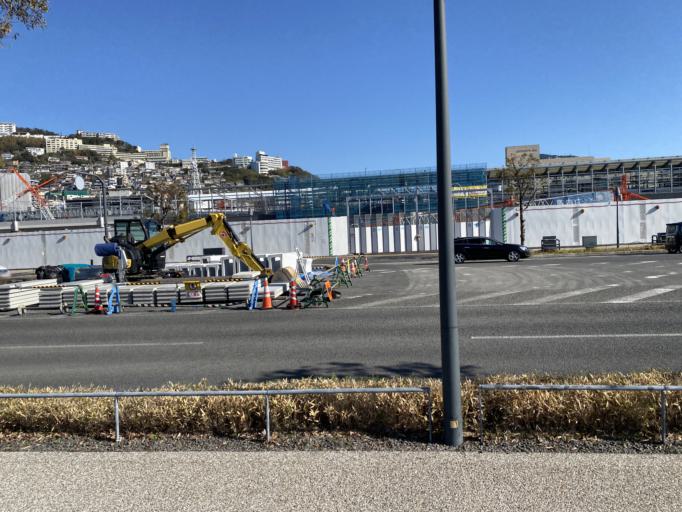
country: JP
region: Nagasaki
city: Nagasaki-shi
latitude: 32.7527
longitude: 129.8669
